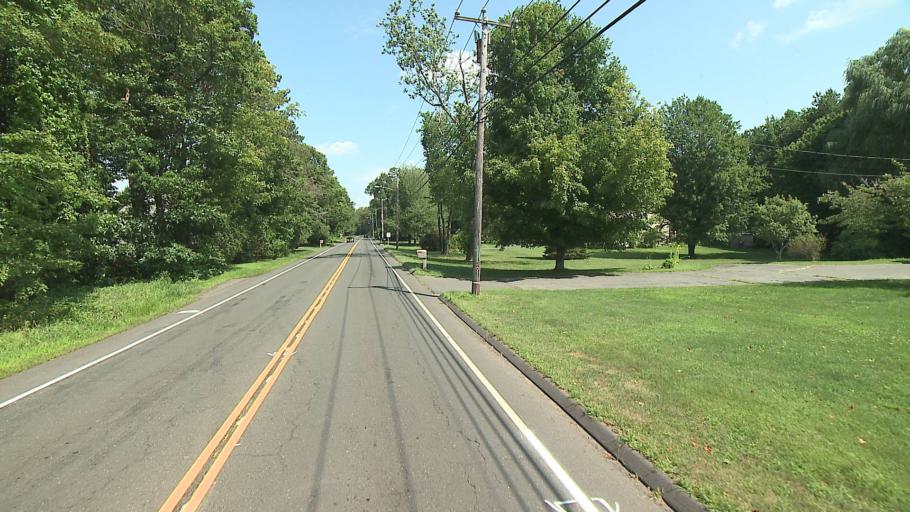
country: US
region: Connecticut
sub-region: Hartford County
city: Plainville
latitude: 41.7145
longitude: -72.8817
